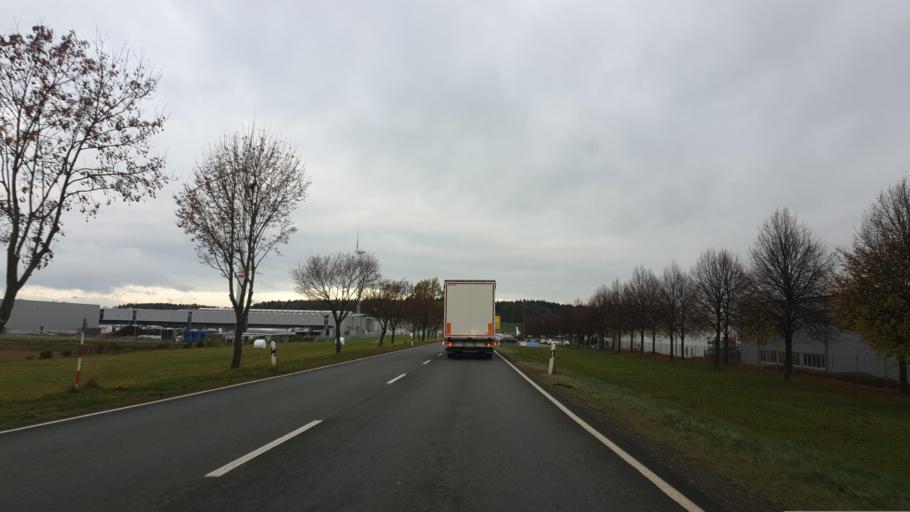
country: DE
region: Saxony
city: Reichenbach/Vogtland
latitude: 50.6003
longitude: 12.3239
